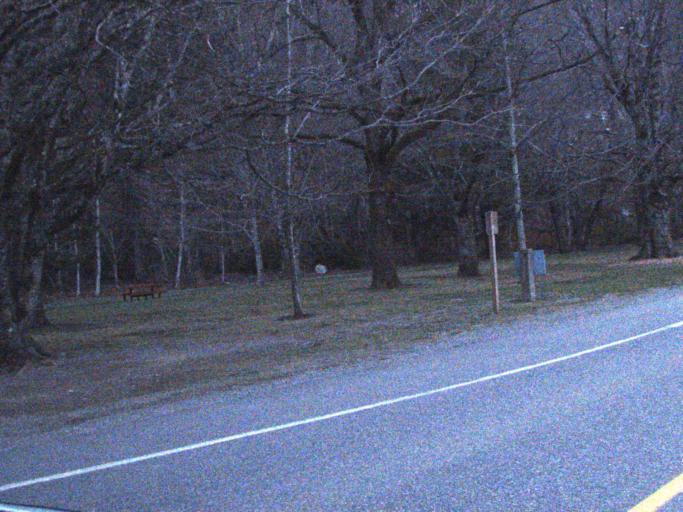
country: US
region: Washington
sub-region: Snohomish County
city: Darrington
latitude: 48.6741
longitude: -121.2455
